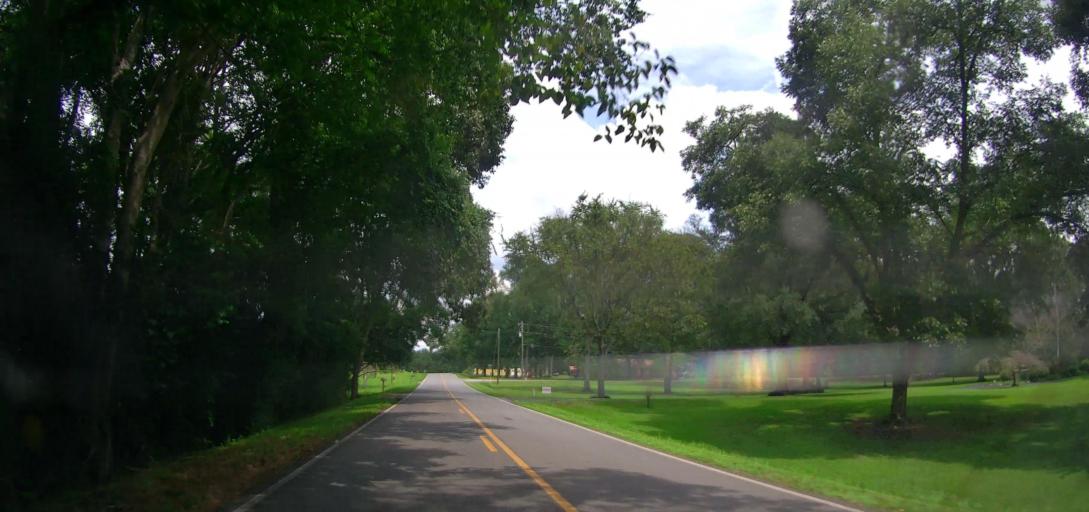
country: US
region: Georgia
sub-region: Houston County
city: Perry
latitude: 32.5153
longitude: -83.7225
